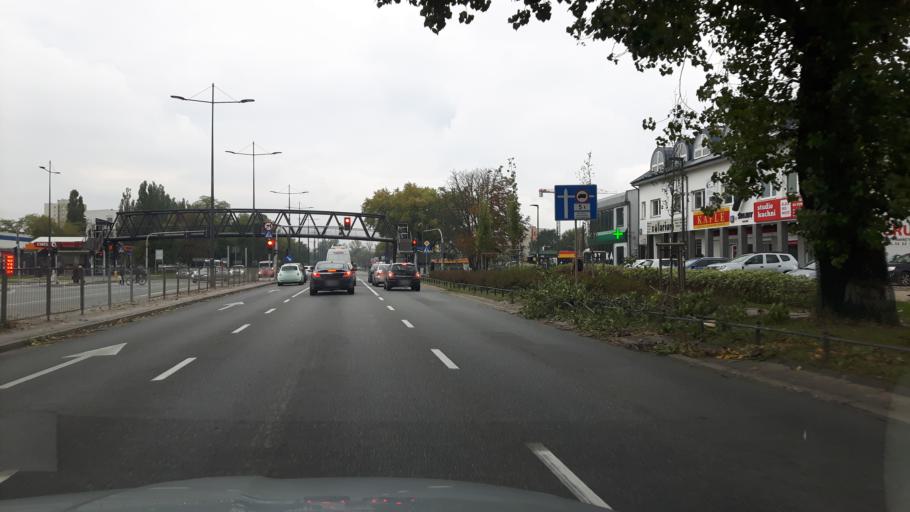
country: PL
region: Masovian Voivodeship
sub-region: Warszawa
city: Praga Poludnie
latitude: 52.2369
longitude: 21.1212
